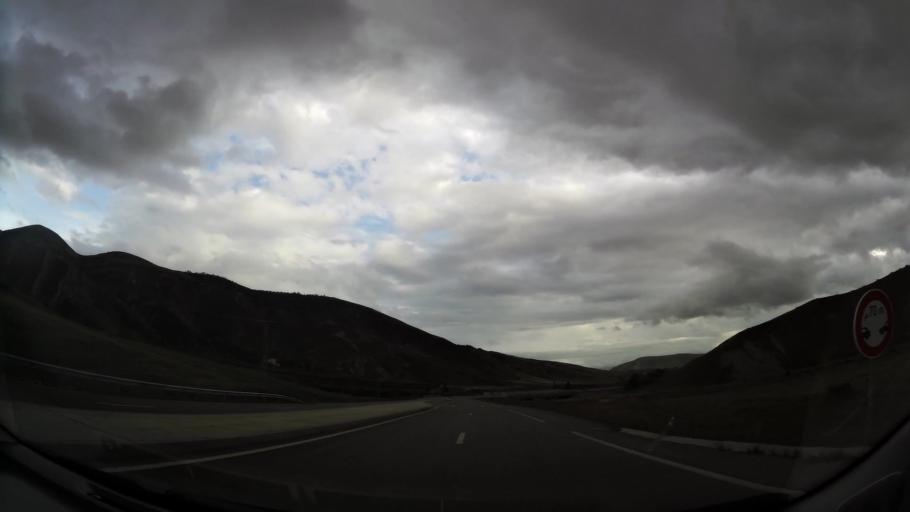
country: MA
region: Taza-Al Hoceima-Taounate
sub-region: Taza
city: Taza
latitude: 34.3238
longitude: -3.9522
